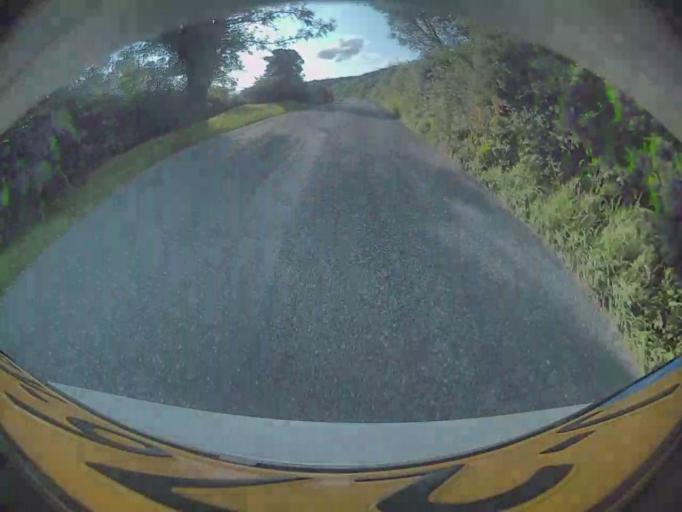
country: IE
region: Leinster
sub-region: Wicklow
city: Enniskerry
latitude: 53.1873
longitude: -6.2200
